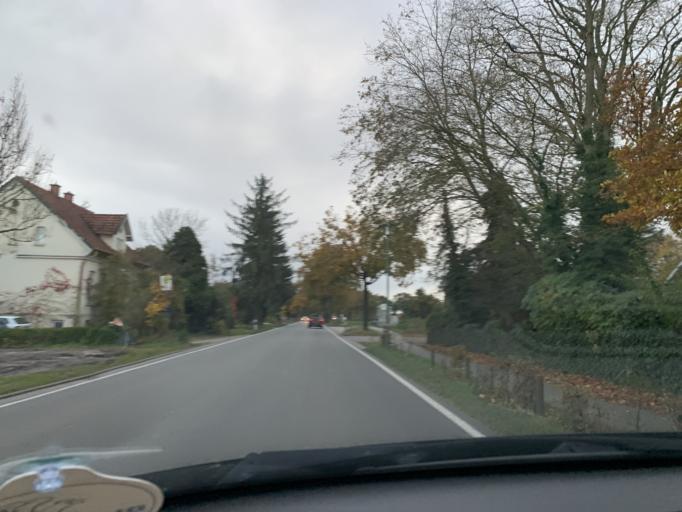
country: DE
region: Lower Saxony
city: Westerstede
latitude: 53.2766
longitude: 7.9609
